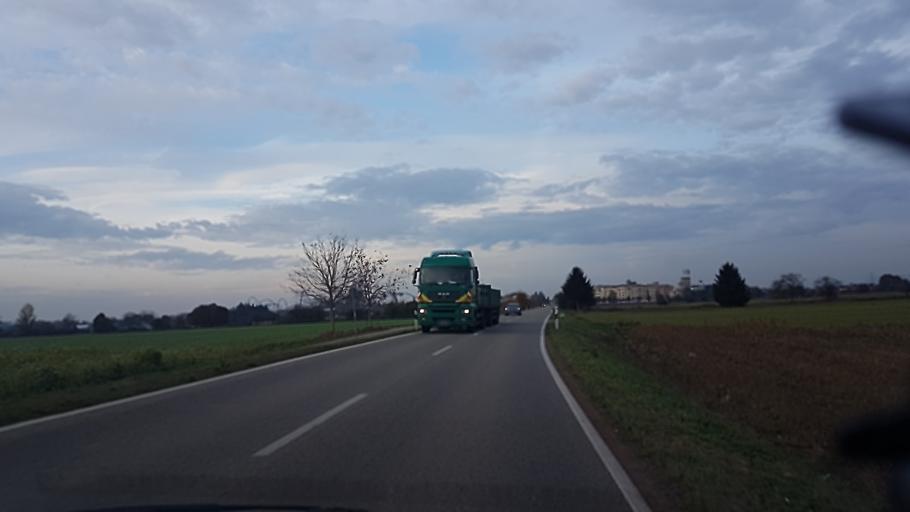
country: DE
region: Baden-Wuerttemberg
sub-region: Freiburg Region
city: Rust
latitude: 48.2528
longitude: 7.7175
